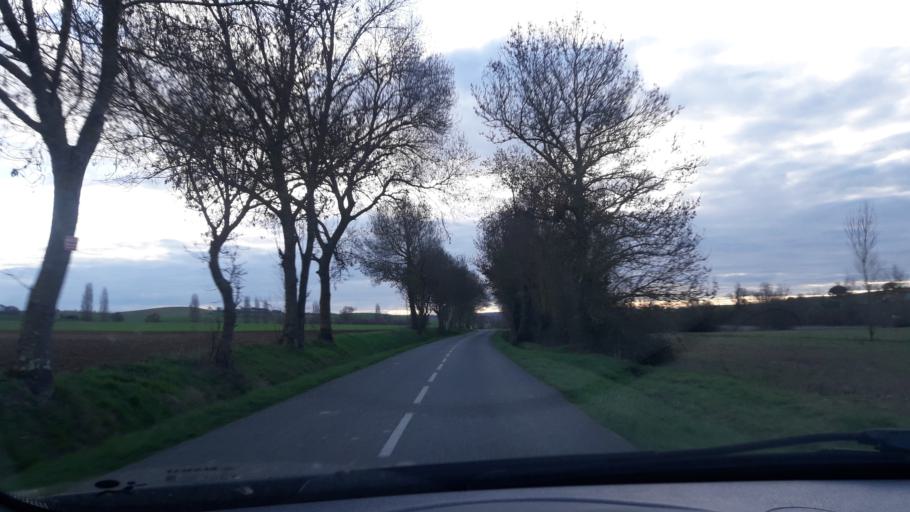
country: FR
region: Midi-Pyrenees
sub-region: Departement du Gers
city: Pujaudran
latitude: 43.6580
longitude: 1.1136
